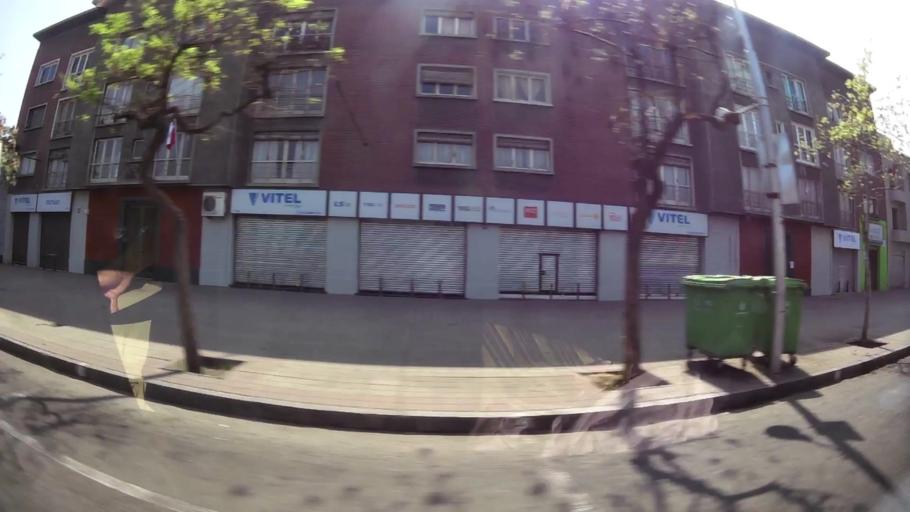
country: CL
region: Santiago Metropolitan
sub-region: Provincia de Santiago
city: Santiago
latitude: -33.4595
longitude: -70.6501
